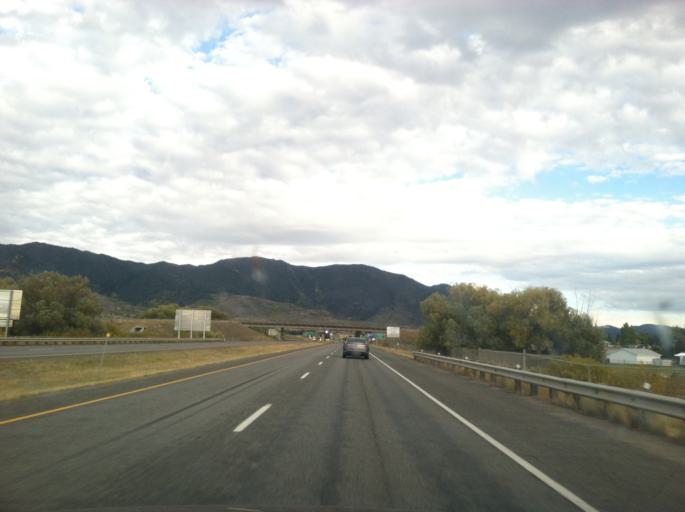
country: US
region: Montana
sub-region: Silver Bow County
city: Butte
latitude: 45.9895
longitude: -112.5243
